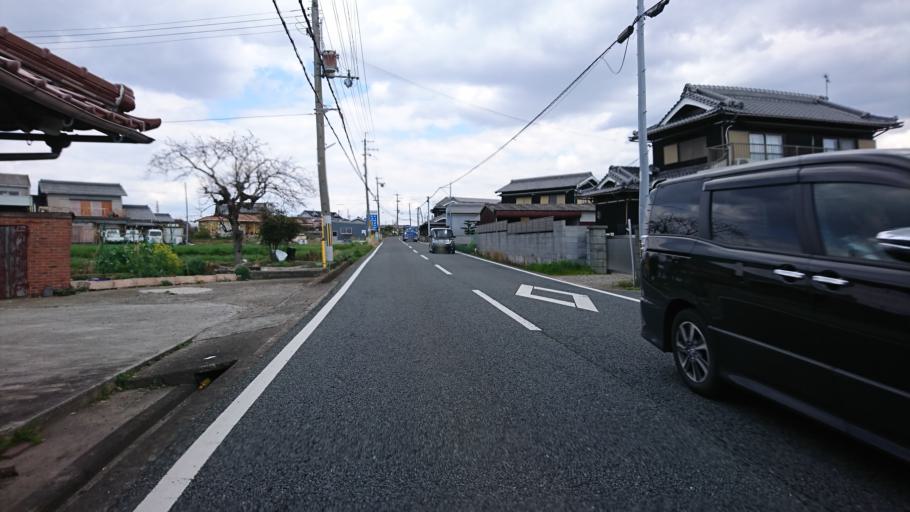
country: JP
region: Hyogo
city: Miki
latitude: 34.7357
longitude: 134.9254
